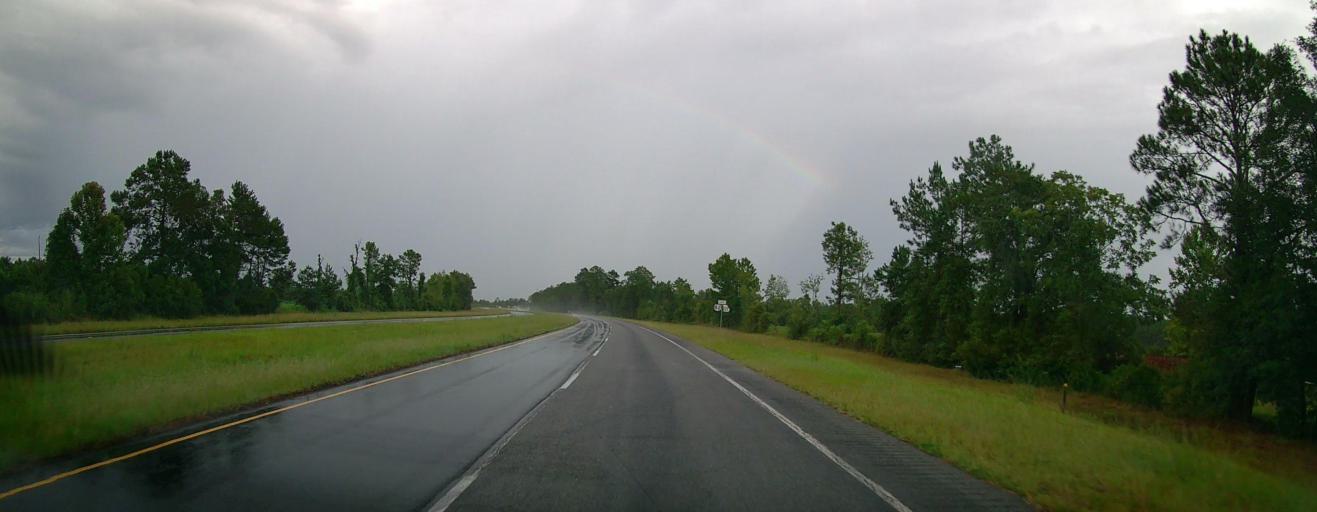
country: US
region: Georgia
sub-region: Ware County
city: Deenwood
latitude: 31.2497
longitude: -82.4474
